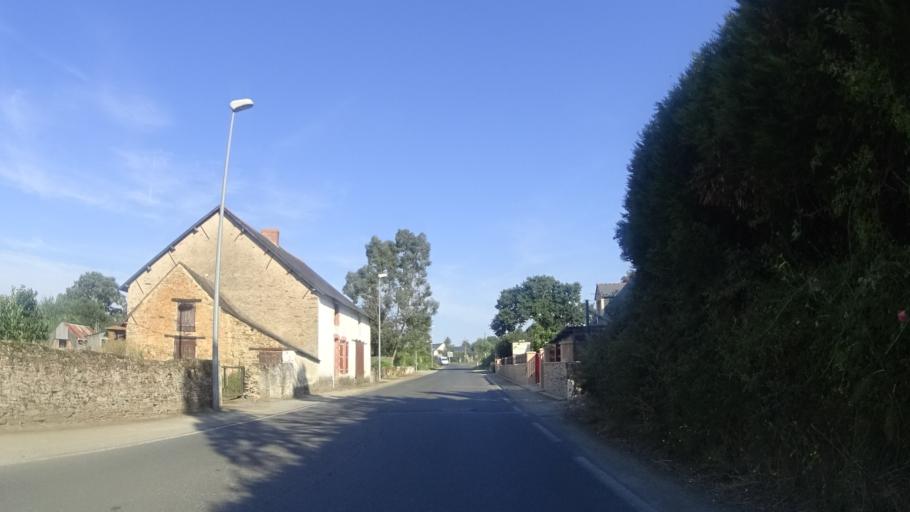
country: FR
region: Pays de la Loire
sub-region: Departement de la Loire-Atlantique
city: Joue-sur-Erdre
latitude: 47.4972
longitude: -1.4239
